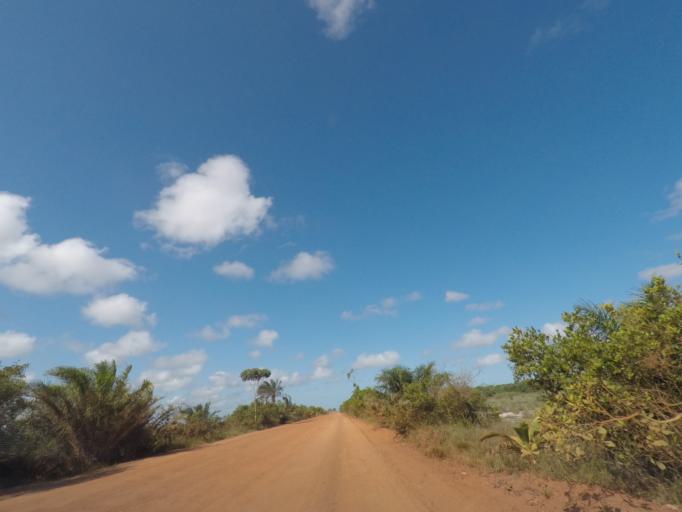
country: BR
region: Bahia
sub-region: Marau
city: Marau
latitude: -14.1787
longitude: -39.0220
